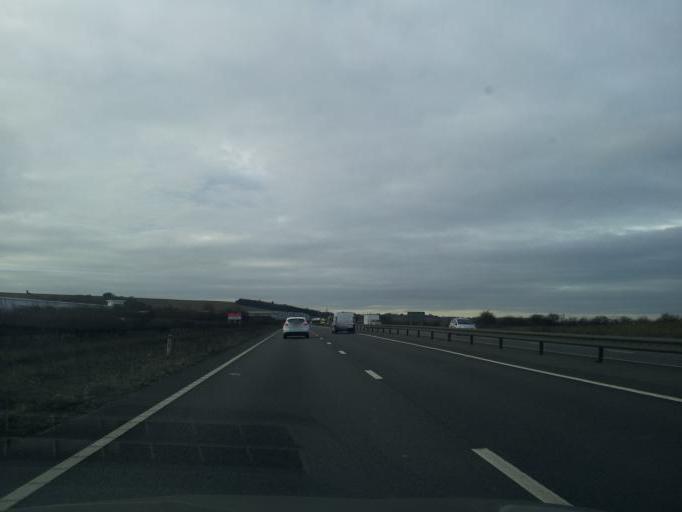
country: GB
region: England
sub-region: Lincolnshire
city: Great Gonerby
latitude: 52.9495
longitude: -0.6821
